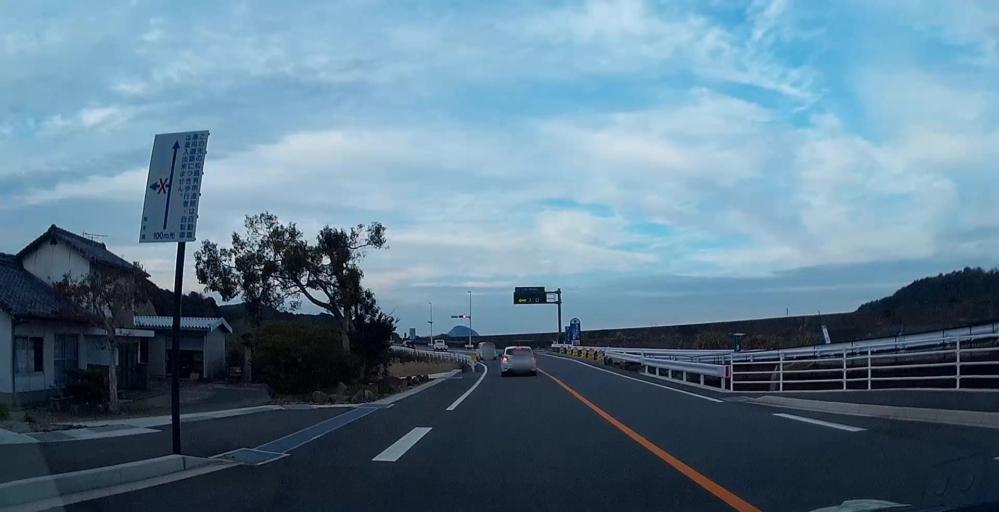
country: JP
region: Kumamoto
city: Hondo
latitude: 32.4985
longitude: 130.3928
